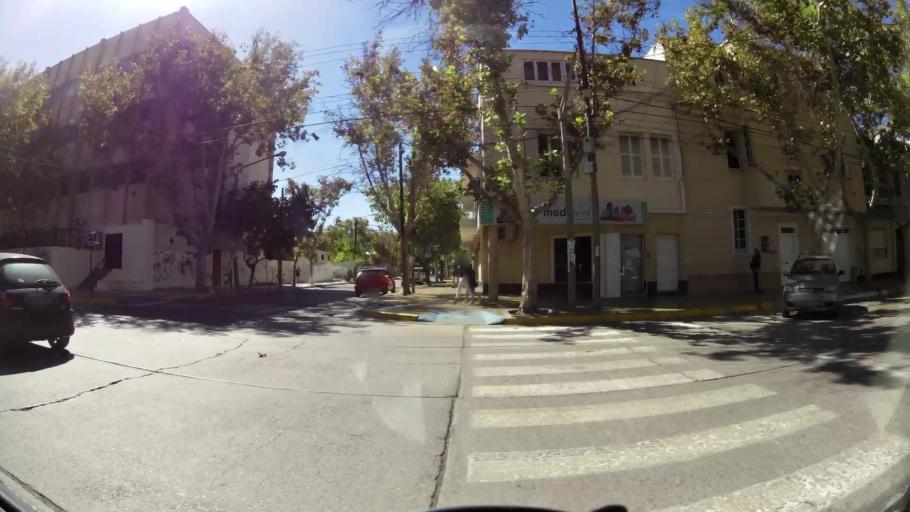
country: AR
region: San Juan
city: San Juan
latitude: -31.5376
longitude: -68.5300
